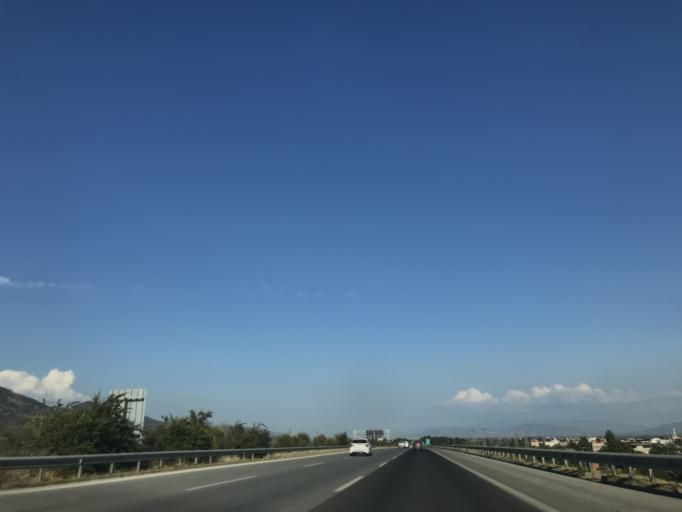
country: TR
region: Aydin
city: Germencik
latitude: 37.8803
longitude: 27.5936
